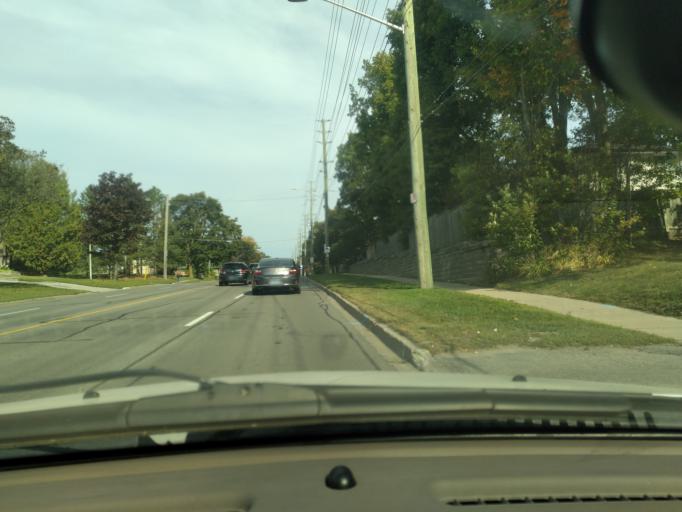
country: CA
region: Ontario
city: Barrie
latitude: 44.3899
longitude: -79.7115
